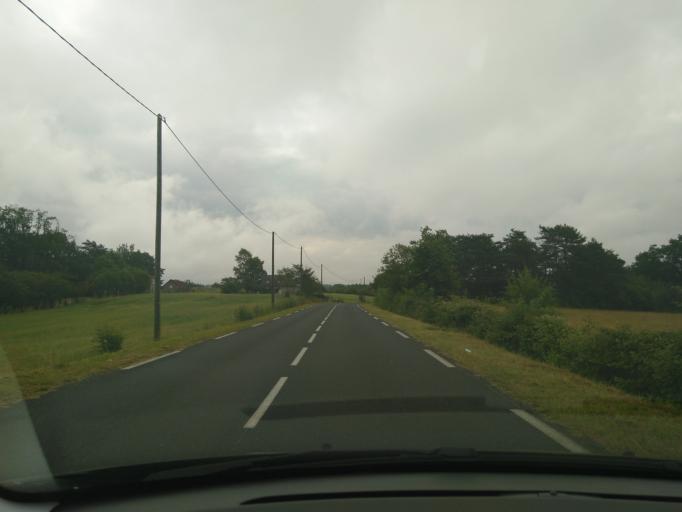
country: FR
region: Limousin
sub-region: Departement de la Correze
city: Cosnac
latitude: 45.1041
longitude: 1.5517
